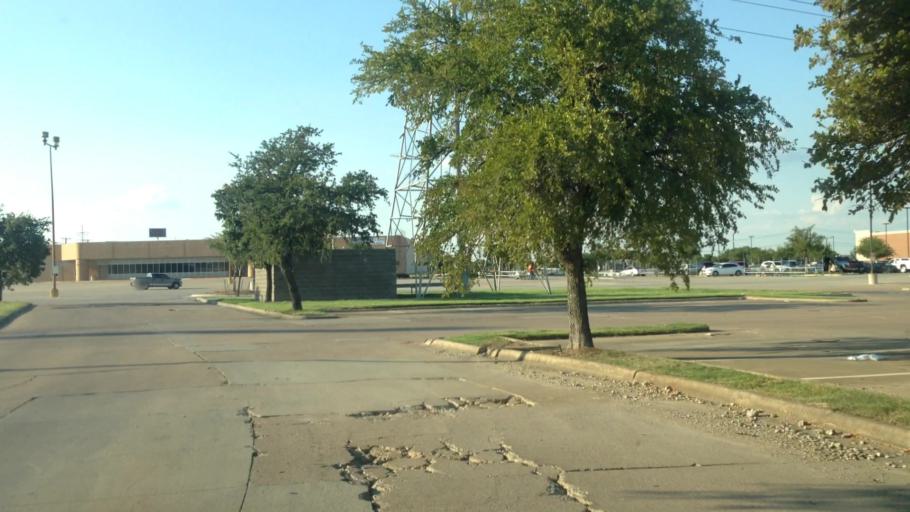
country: US
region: Texas
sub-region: Tarrant County
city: North Richland Hills
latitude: 32.8414
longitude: -97.2366
